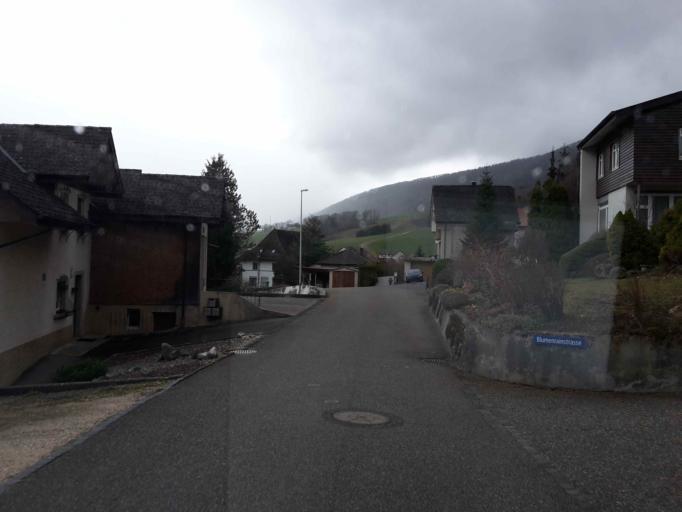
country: CH
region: Solothurn
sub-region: Bezirk Thal
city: Welschenrohr
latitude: 47.2817
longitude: 7.5271
